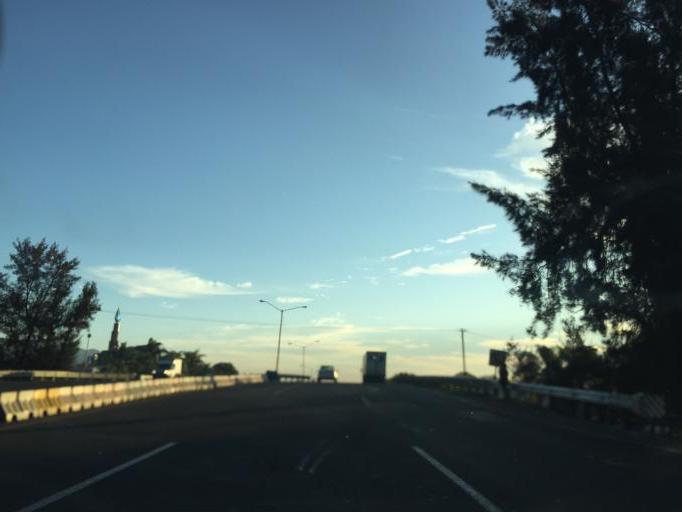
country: MX
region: Veracruz
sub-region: Fortin
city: Fortin de las Flores
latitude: 18.9072
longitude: -96.9987
